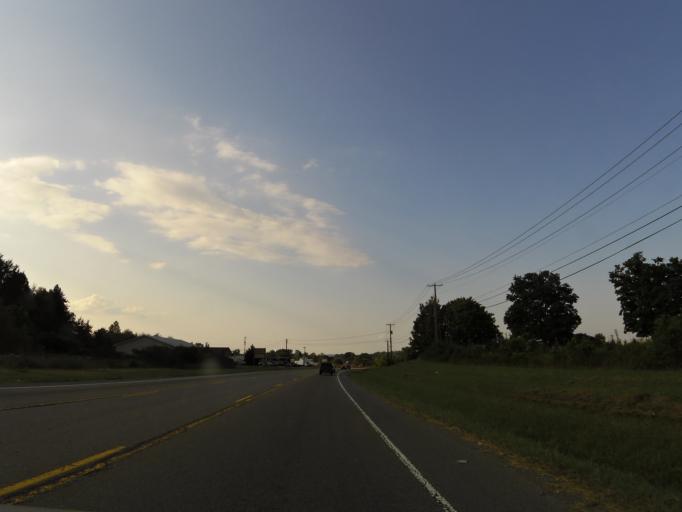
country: US
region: Tennessee
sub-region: Knox County
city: Knoxville
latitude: 35.9685
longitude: -83.8276
